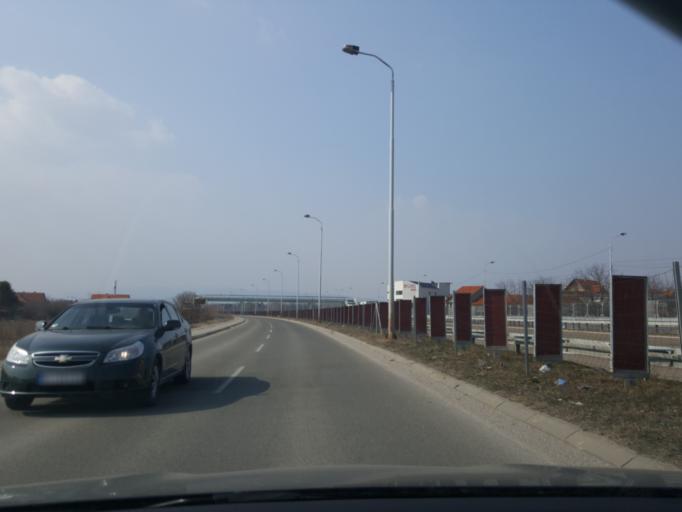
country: RS
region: Central Serbia
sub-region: Nisavski Okrug
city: Nis
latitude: 43.3458
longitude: 21.8768
